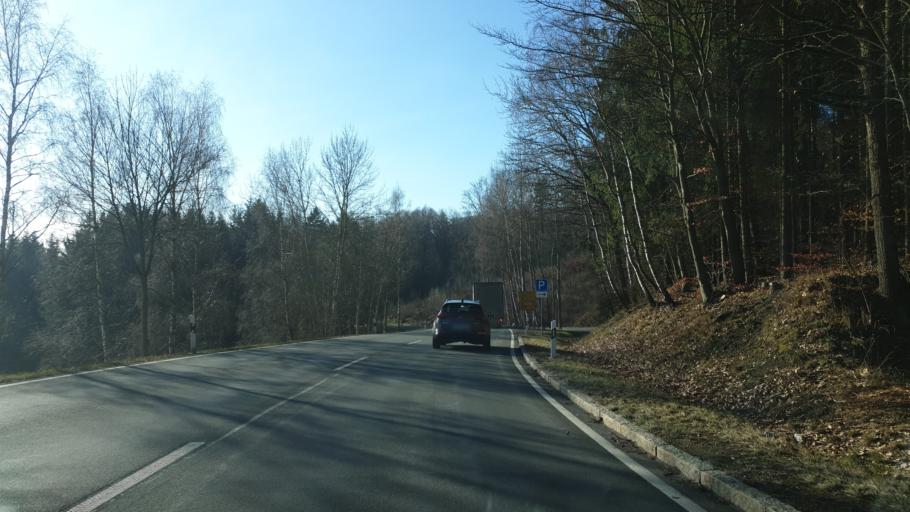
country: DE
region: Saxony
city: Bad Brambach
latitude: 50.1873
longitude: 12.3118
